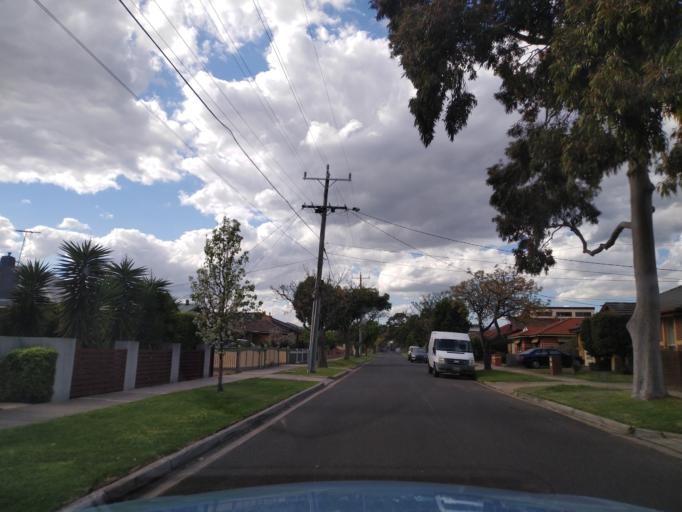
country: AU
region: Victoria
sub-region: Hobsons Bay
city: South Kingsville
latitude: -37.8440
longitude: 144.8652
